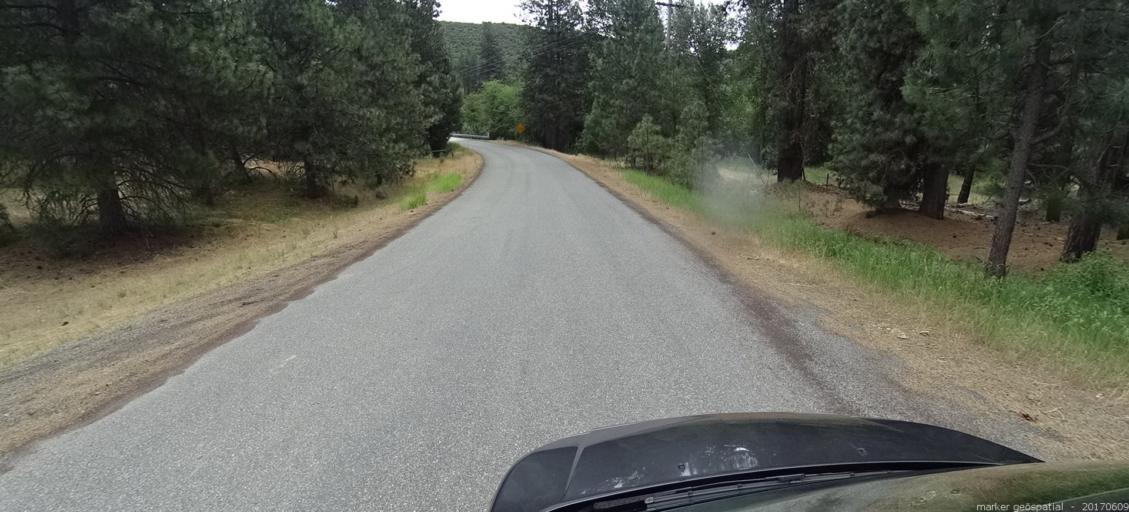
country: US
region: California
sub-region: Siskiyou County
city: Yreka
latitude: 41.4038
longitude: -122.8684
